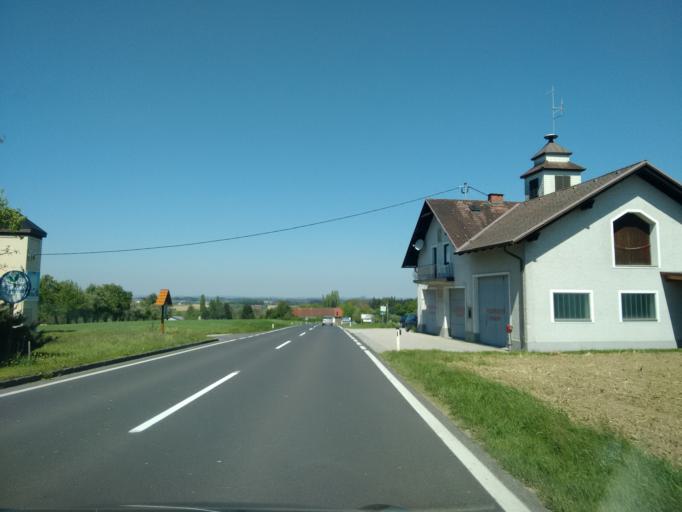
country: AT
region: Upper Austria
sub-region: Politischer Bezirk Kirchdorf an der Krems
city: Kremsmunster
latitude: 48.0619
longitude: 14.1031
